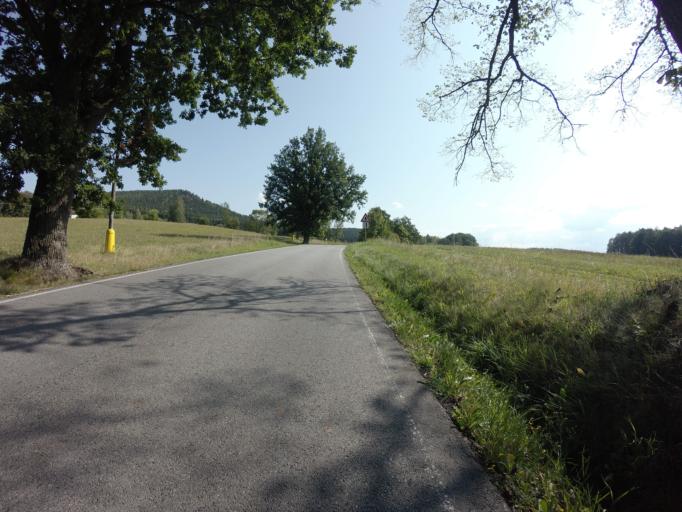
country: CZ
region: Jihocesky
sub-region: Okres Cesky Krumlov
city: Vyssi Brod
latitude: 48.6244
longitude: 14.3142
